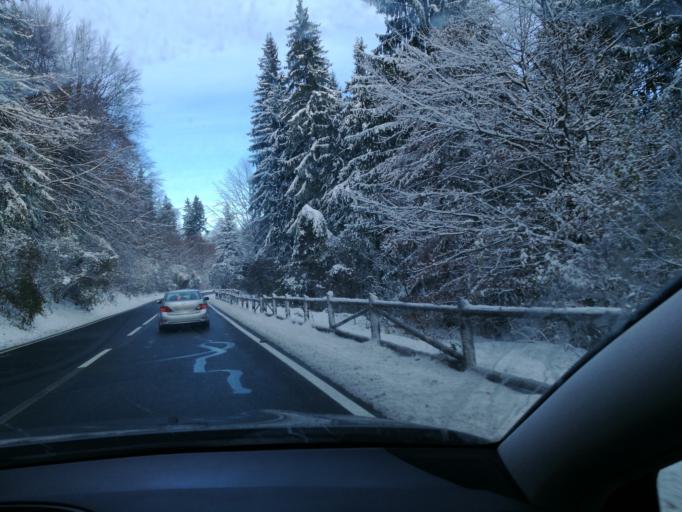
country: RO
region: Brasov
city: Brasov
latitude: 45.6274
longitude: 25.5502
